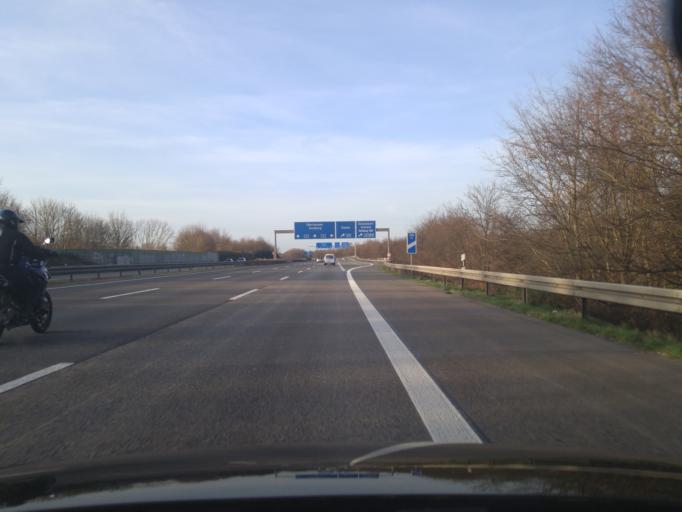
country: DE
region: North Rhine-Westphalia
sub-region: Regierungsbezirk Dusseldorf
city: Ratingen
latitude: 51.3429
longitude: 6.8688
